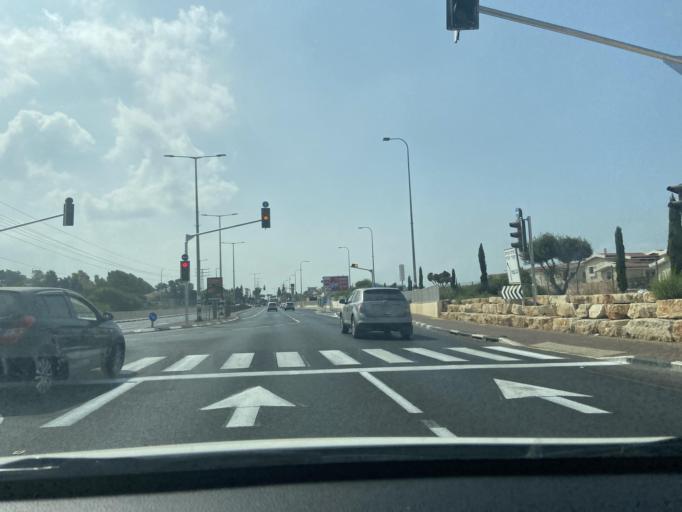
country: IL
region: Northern District
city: El Mazra`a
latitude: 32.9956
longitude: 35.0974
